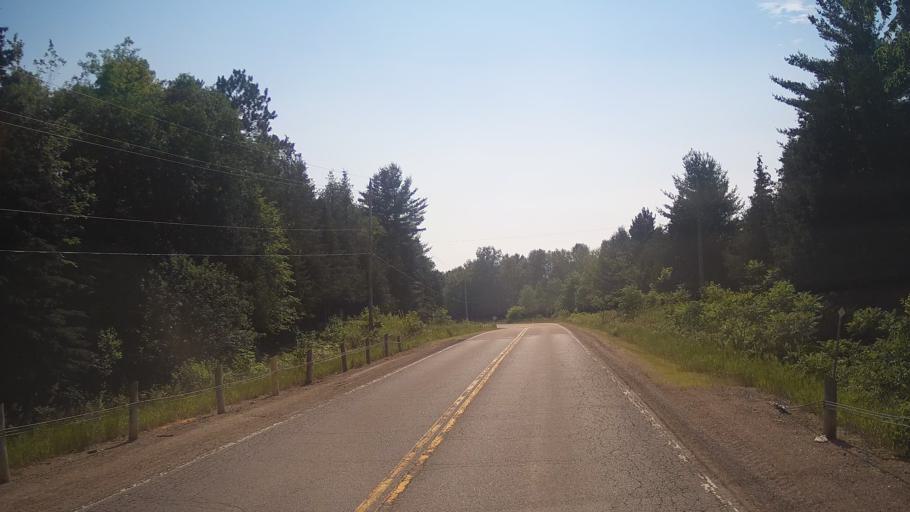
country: CA
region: Ontario
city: Pembroke
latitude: 45.6034
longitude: -77.2293
